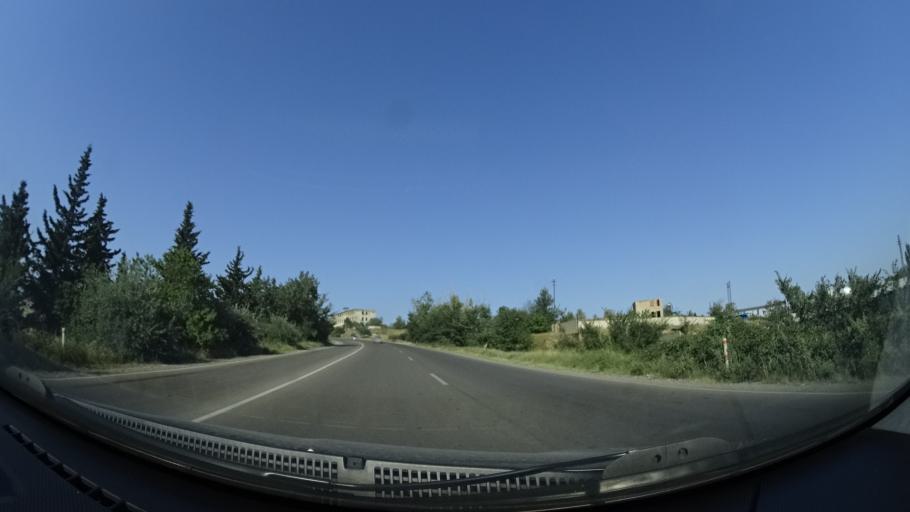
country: GE
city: Didi Lilo
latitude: 41.6933
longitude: 45.0362
